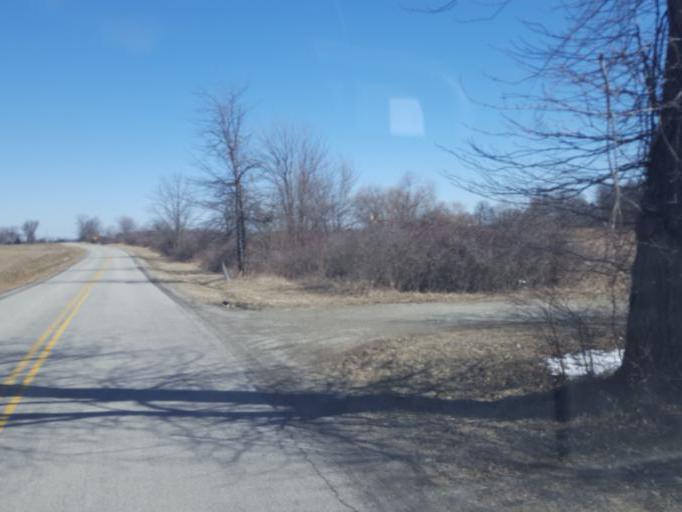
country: US
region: Ohio
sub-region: Wyandot County
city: Upper Sandusky
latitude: 40.7338
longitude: -83.2945
